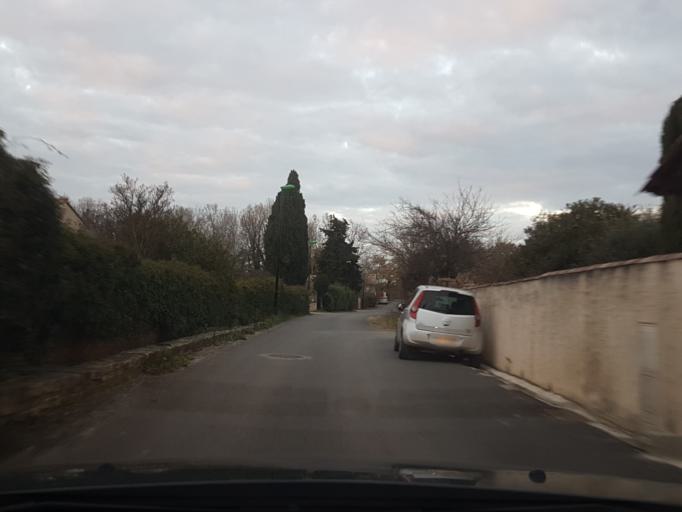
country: FR
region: Provence-Alpes-Cote d'Azur
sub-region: Departement du Vaucluse
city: Loriol-du-Comtat
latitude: 44.0786
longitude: 4.9999
